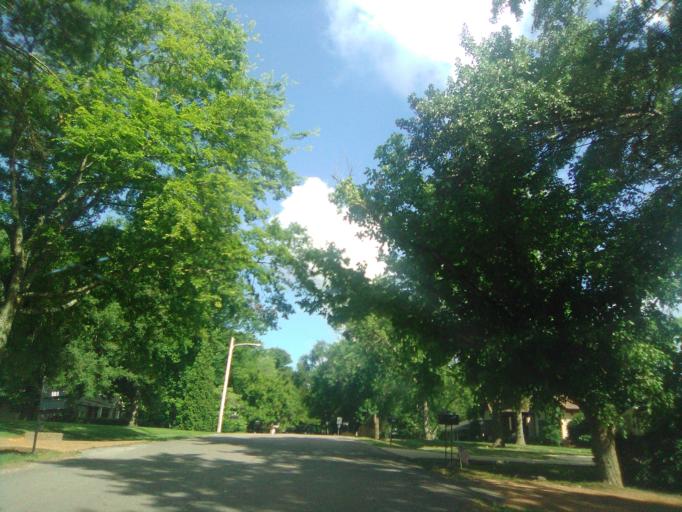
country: US
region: Tennessee
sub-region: Davidson County
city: Belle Meade
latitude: 36.1029
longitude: -86.8709
